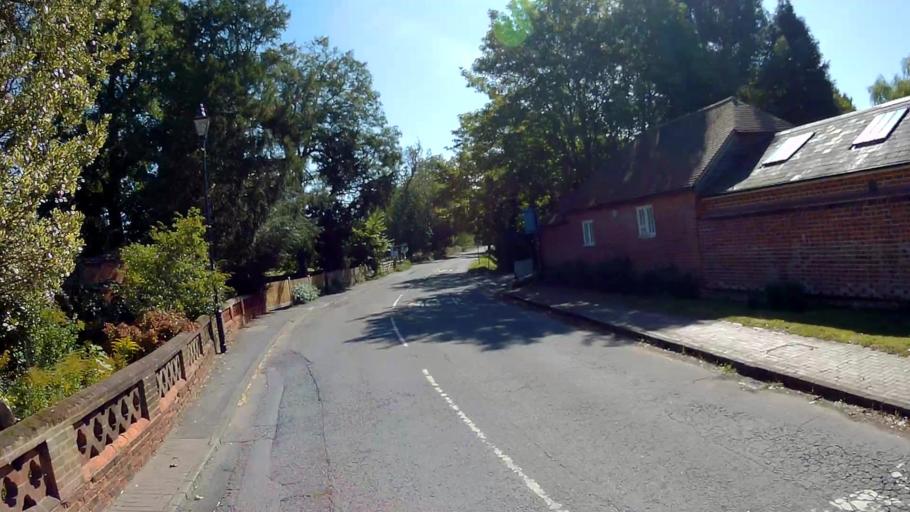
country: GB
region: England
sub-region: Wokingham
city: Swallowfield
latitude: 51.3793
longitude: -0.9563
